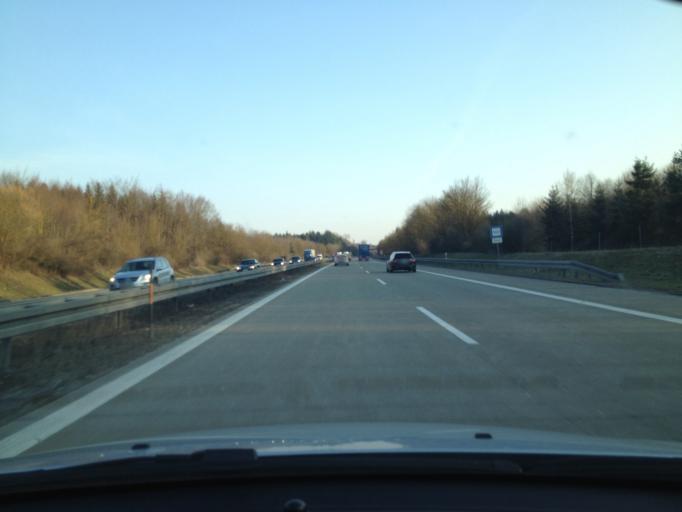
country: DE
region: Baden-Wuerttemberg
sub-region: Regierungsbezirk Stuttgart
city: Nattheim
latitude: 48.7154
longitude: 10.2095
